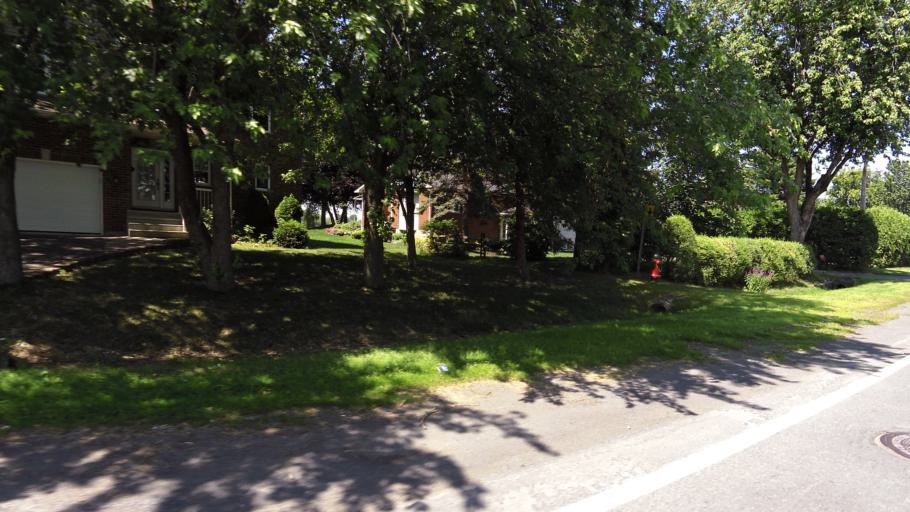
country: CA
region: Quebec
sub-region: Monteregie
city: Saint-Jean-sur-Richelieu
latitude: 45.3209
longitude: -73.2508
